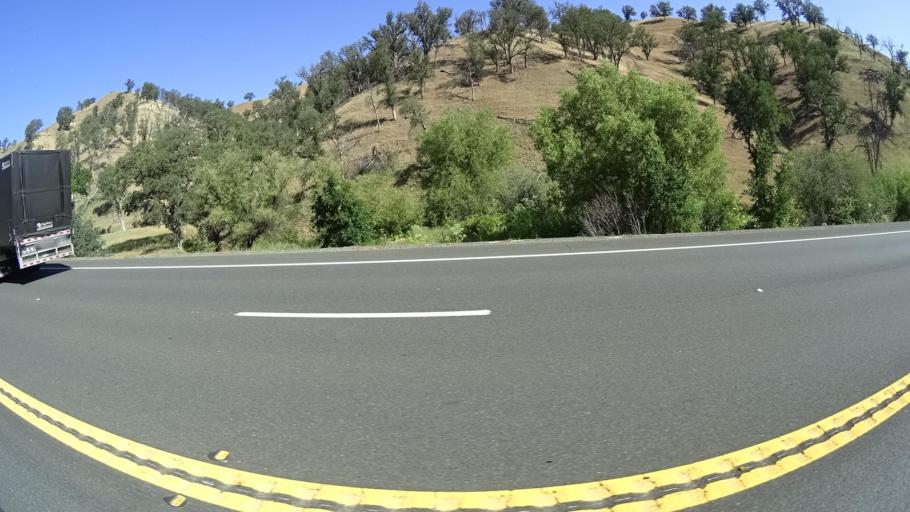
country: US
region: California
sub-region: Lake County
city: Clearlake
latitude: 39.0177
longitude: -122.5816
